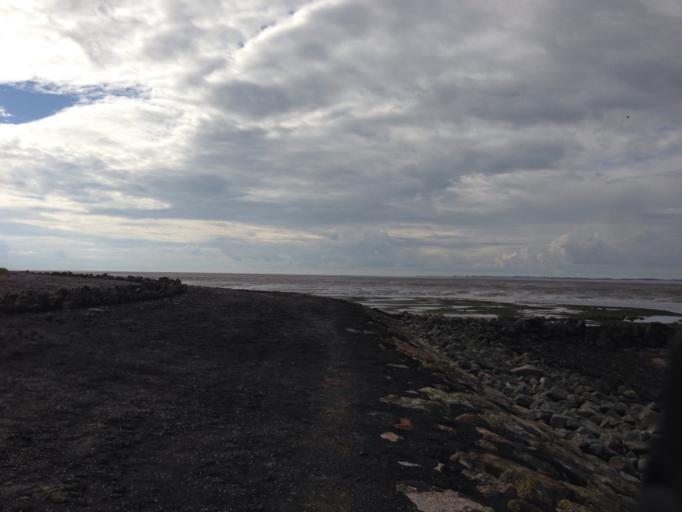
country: DE
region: Schleswig-Holstein
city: Dunsum
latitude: 54.7459
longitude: 8.4280
